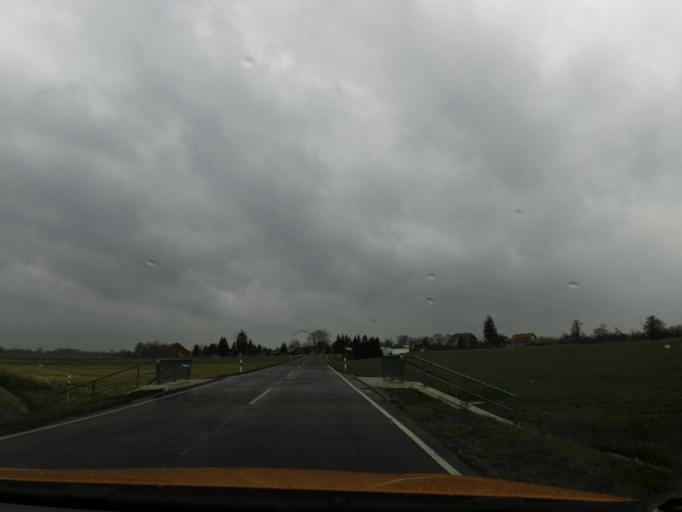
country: DE
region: Brandenburg
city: Ziesar
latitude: 52.2712
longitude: 12.3056
